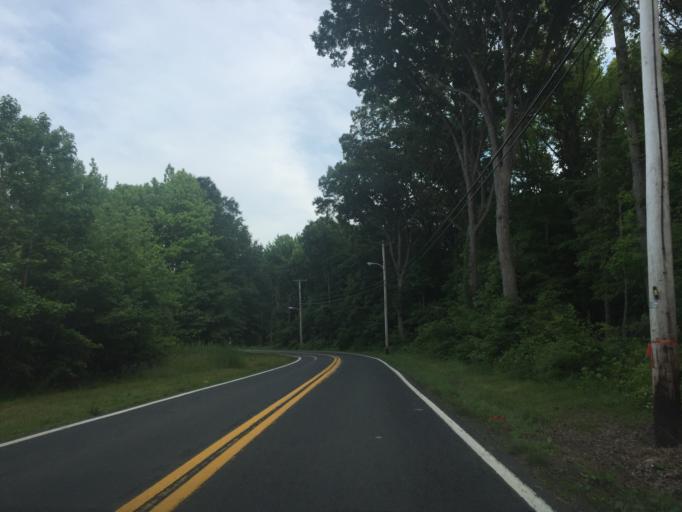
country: US
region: Maryland
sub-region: Baltimore County
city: Edgemere
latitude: 39.2286
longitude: -76.4265
